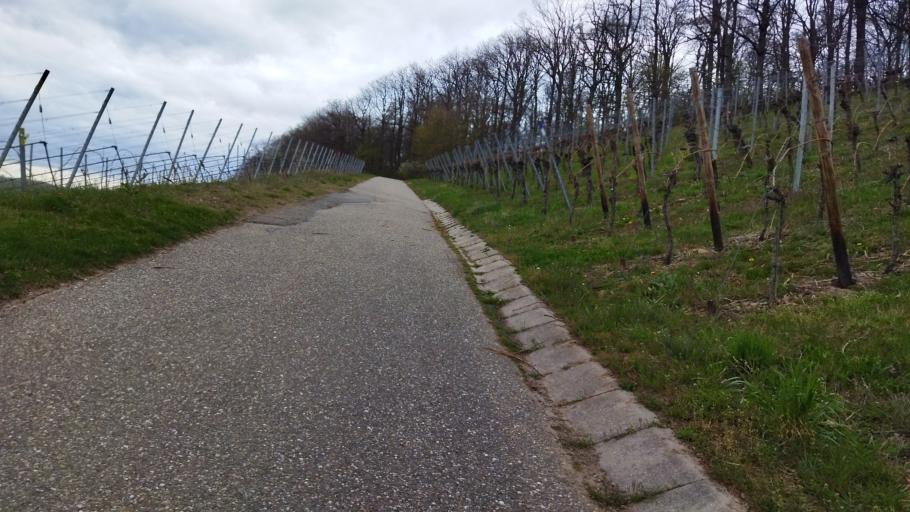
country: DE
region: Baden-Wuerttemberg
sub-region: Regierungsbezirk Stuttgart
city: Erlenbach
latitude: 49.1920
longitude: 9.2792
